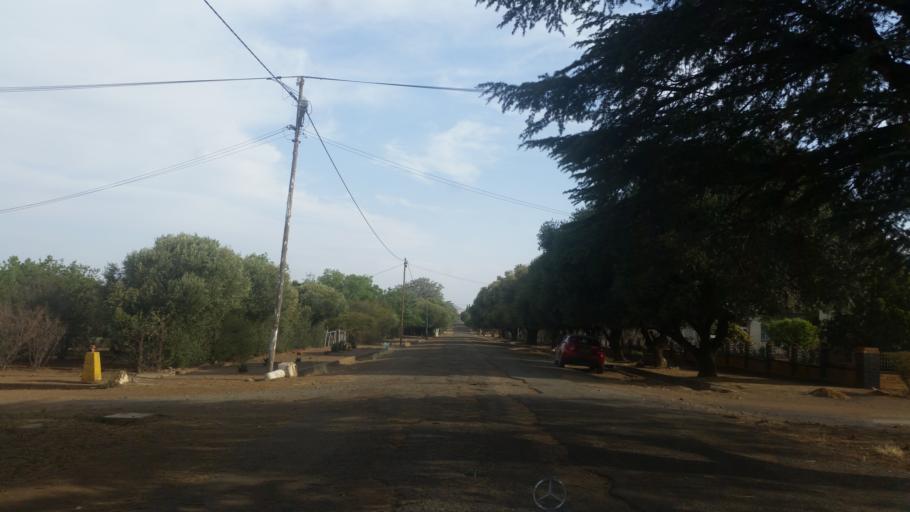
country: ZA
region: Orange Free State
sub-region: Xhariep District Municipality
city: Trompsburg
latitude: -30.4934
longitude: 25.9715
